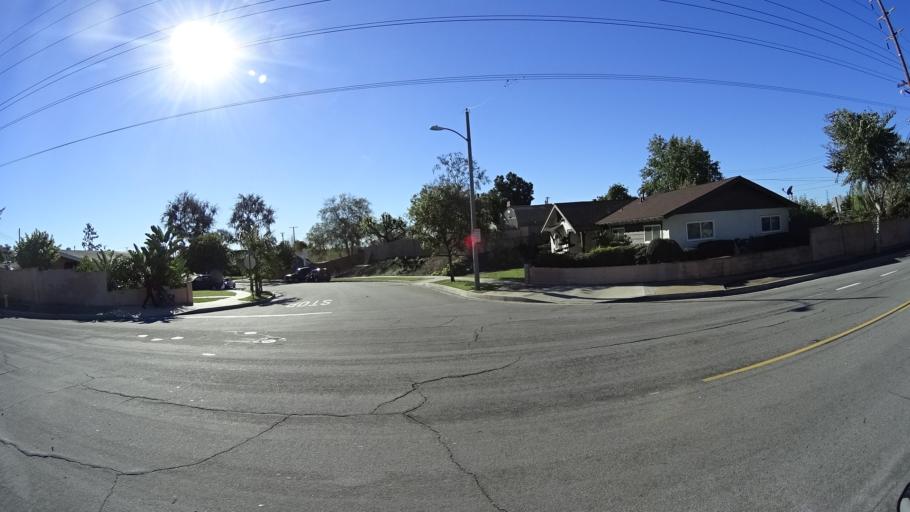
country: US
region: California
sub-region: Orange County
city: La Habra
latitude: 33.9392
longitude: -117.9301
